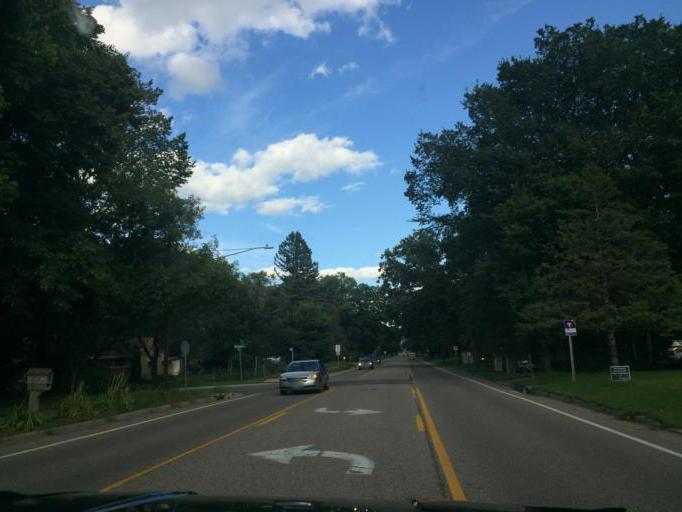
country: US
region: Minnesota
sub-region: Ramsey County
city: Roseville
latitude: 45.0064
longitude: -93.1435
